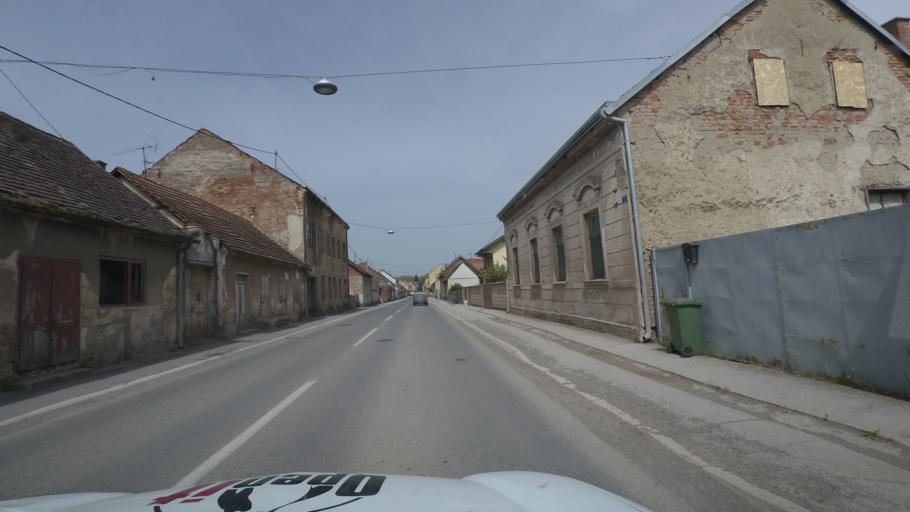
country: HR
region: Sisacko-Moslavacka
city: Glina
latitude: 45.3357
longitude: 16.0953
